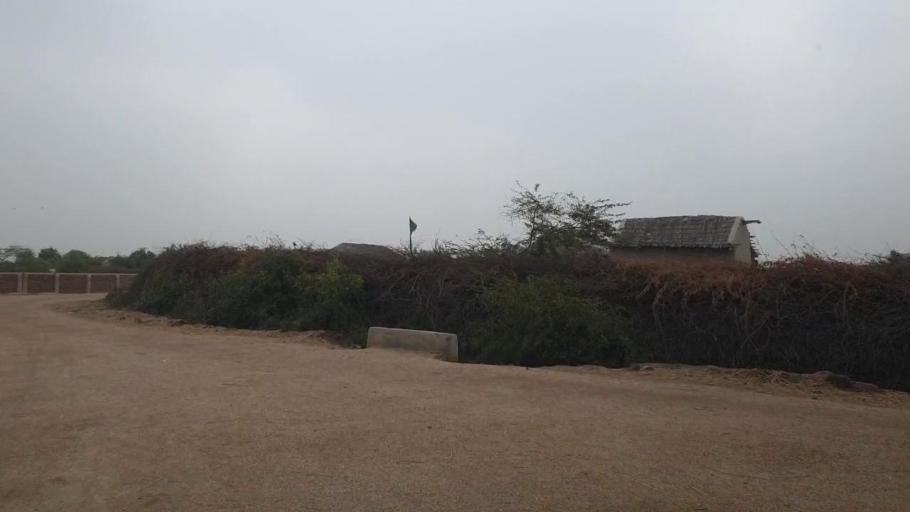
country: PK
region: Sindh
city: Badin
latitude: 24.5683
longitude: 68.6638
